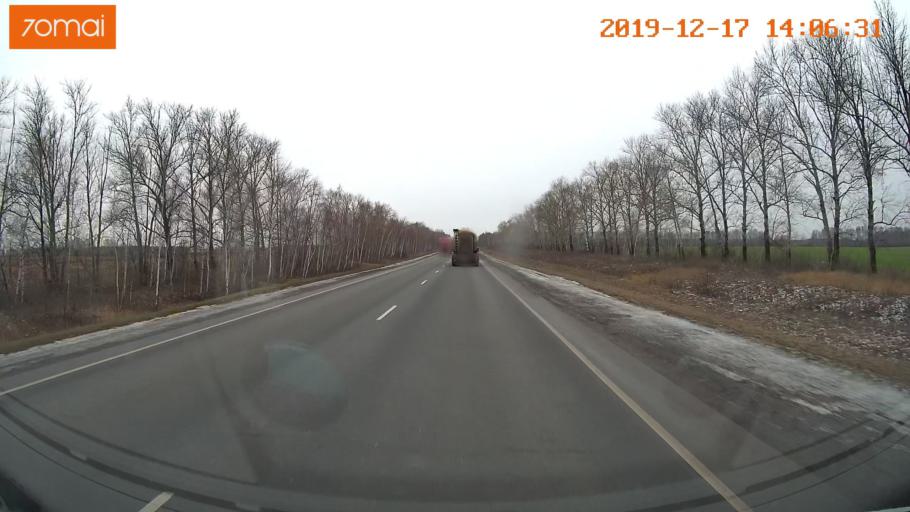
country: RU
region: Rjazan
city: Ryazan'
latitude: 54.5805
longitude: 39.5885
